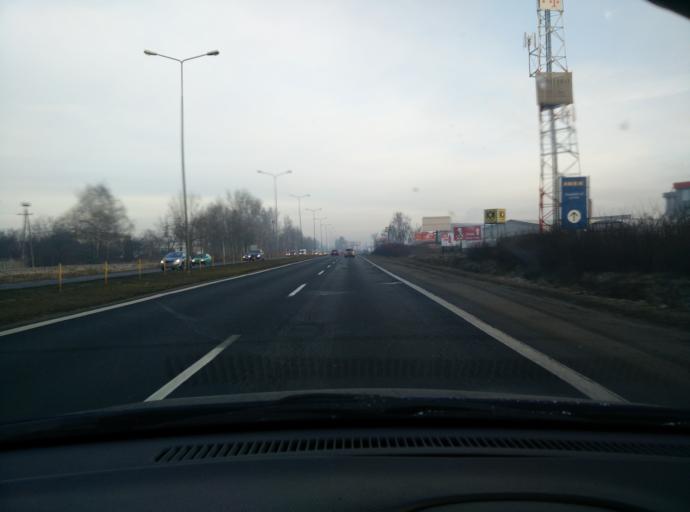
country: PL
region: Greater Poland Voivodeship
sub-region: Powiat poznanski
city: Daszewice
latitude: 52.3639
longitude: 16.9930
